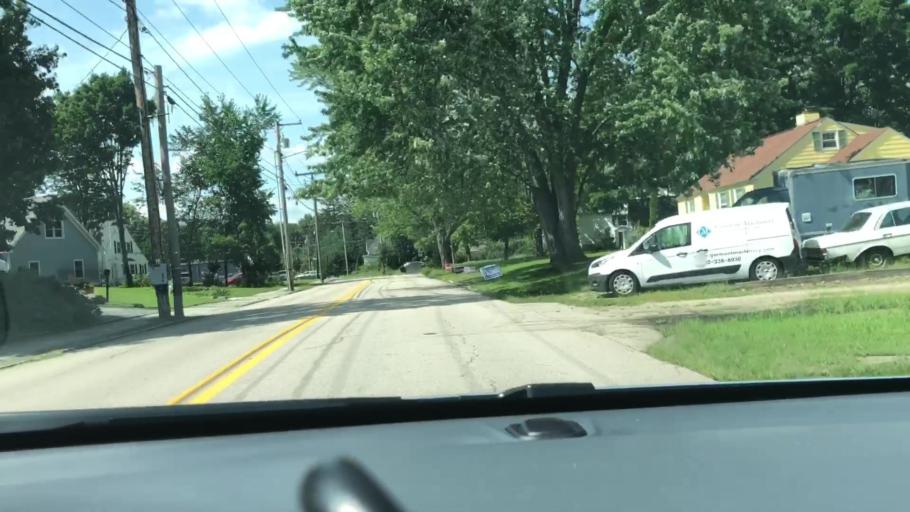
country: US
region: New Hampshire
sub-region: Hillsborough County
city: Pinardville
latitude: 42.9793
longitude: -71.4907
